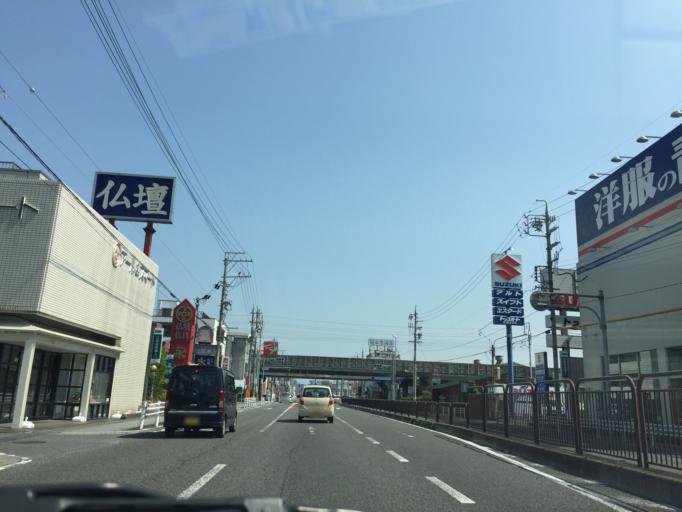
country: JP
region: Gifu
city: Ogaki
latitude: 35.3453
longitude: 136.6224
